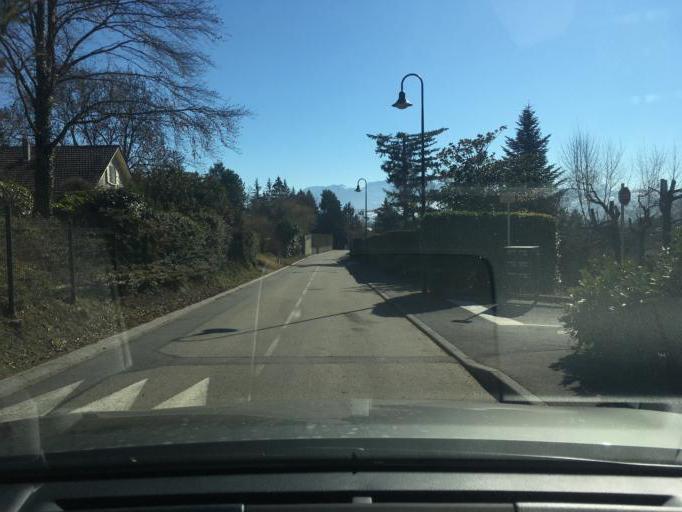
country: FR
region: Rhone-Alpes
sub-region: Departement de la Haute-Savoie
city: Vetraz-Monthoux
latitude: 46.1786
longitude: 6.2583
